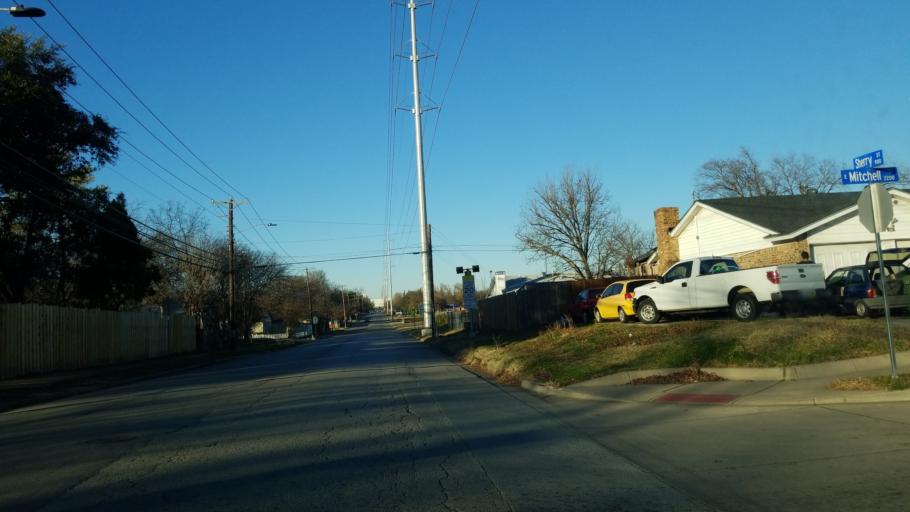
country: US
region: Texas
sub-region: Tarrant County
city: Arlington
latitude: 32.7248
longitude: -97.0717
